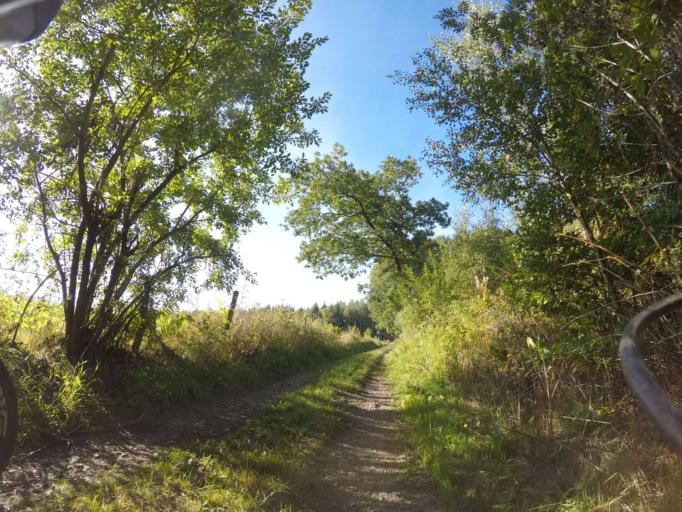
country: BE
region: Wallonia
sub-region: Province du Luxembourg
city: Fauvillers
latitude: 49.9368
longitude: 5.6616
